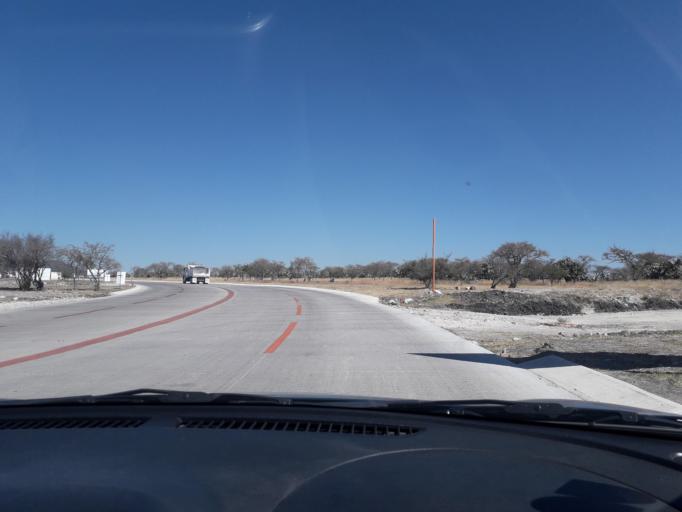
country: MX
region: Queretaro
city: Santa Rosa Jauregui
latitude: 20.7330
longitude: -100.4826
